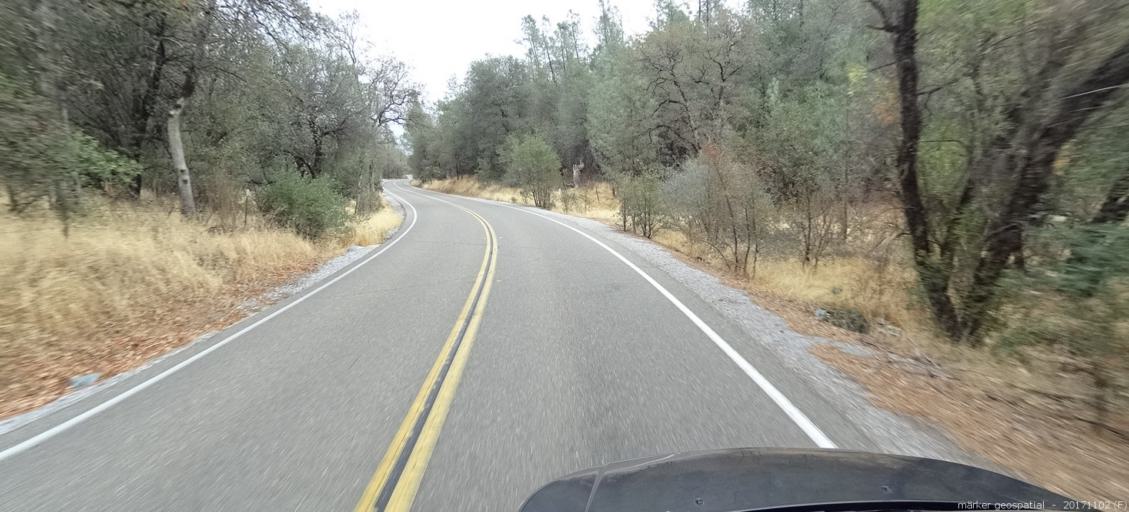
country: US
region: California
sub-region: Shasta County
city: Bella Vista
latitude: 40.7046
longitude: -122.2583
